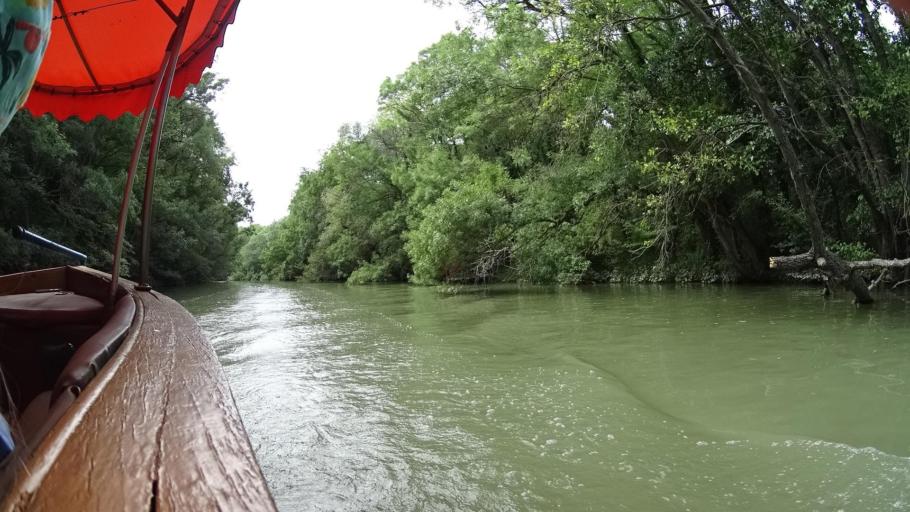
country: BG
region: Varna
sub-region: Obshtina Byala
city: Byala
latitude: 43.0231
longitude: 27.8691
